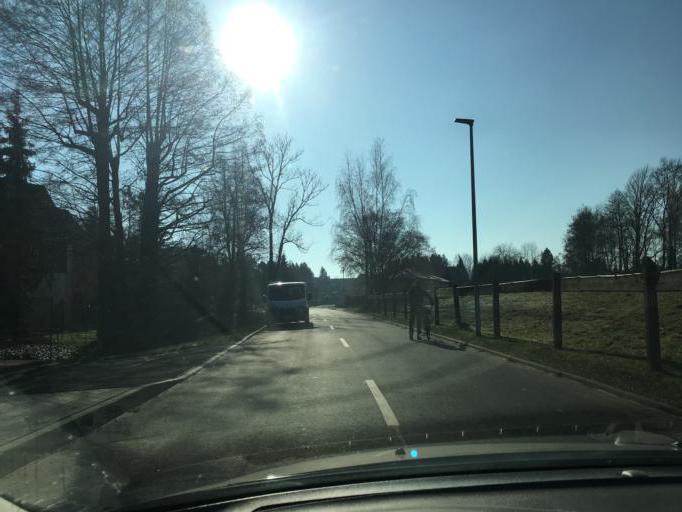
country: DE
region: Saxony
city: Geithain
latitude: 51.0393
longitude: 12.7107
